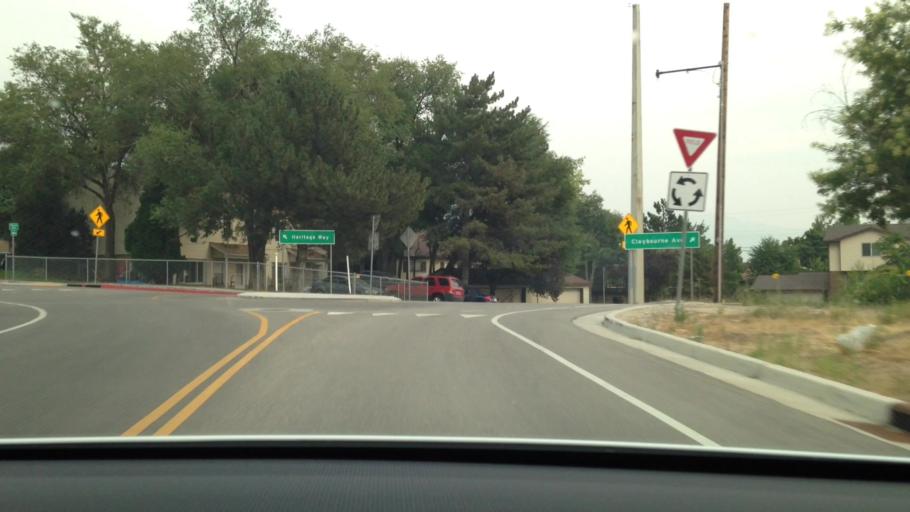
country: US
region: Utah
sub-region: Salt Lake County
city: Canyon Rim
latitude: 40.7115
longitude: -111.8234
